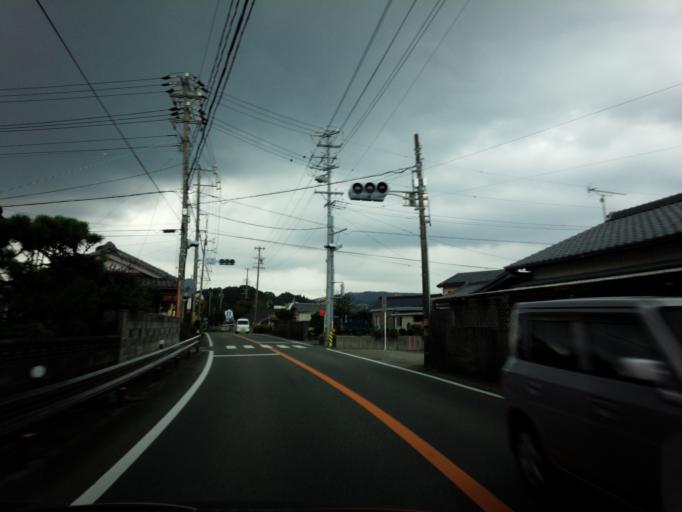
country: JP
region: Mie
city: Toba
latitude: 34.3661
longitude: 136.8087
